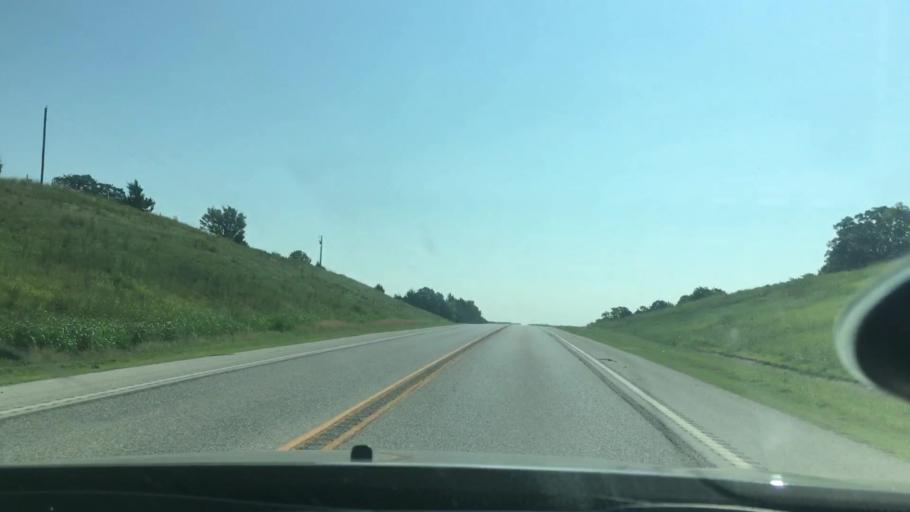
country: US
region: Oklahoma
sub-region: Carter County
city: Dickson
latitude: 34.0979
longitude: -96.9545
